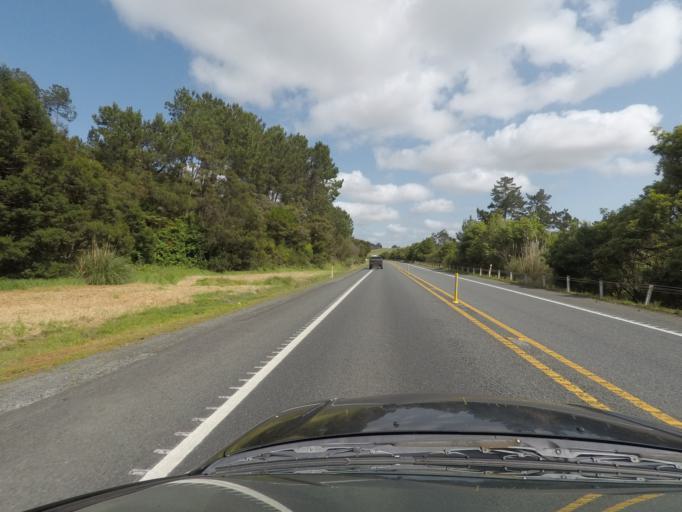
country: NZ
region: Northland
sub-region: Whangarei
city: Whangarei
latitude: -35.8231
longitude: 174.3061
